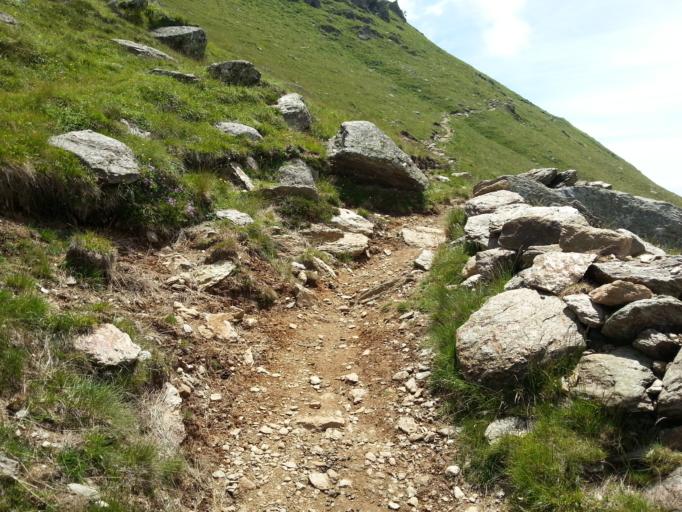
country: CH
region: Ticino
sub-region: Lugano District
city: Tesserete
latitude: 46.1009
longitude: 8.9845
